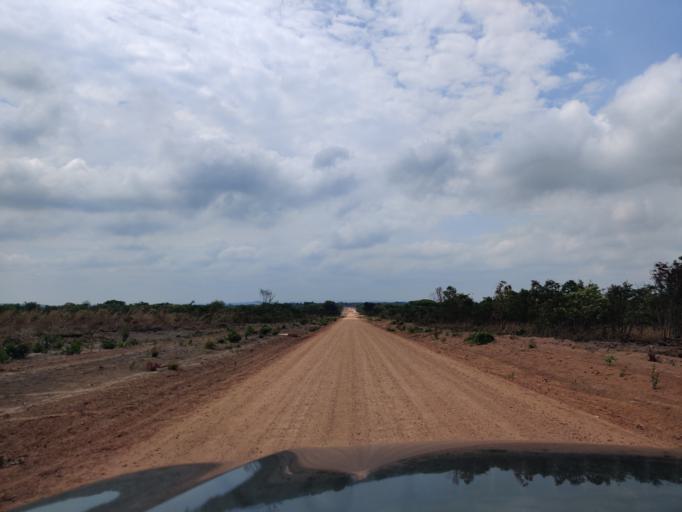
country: ZM
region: Central
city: Mkushi
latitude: -13.6779
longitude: 29.7535
